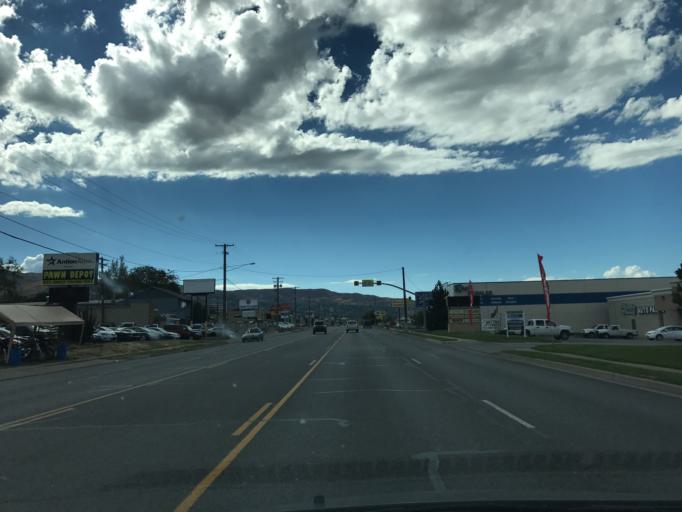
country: US
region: Utah
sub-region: Davis County
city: Woods Cross
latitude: 40.8824
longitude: -111.8923
